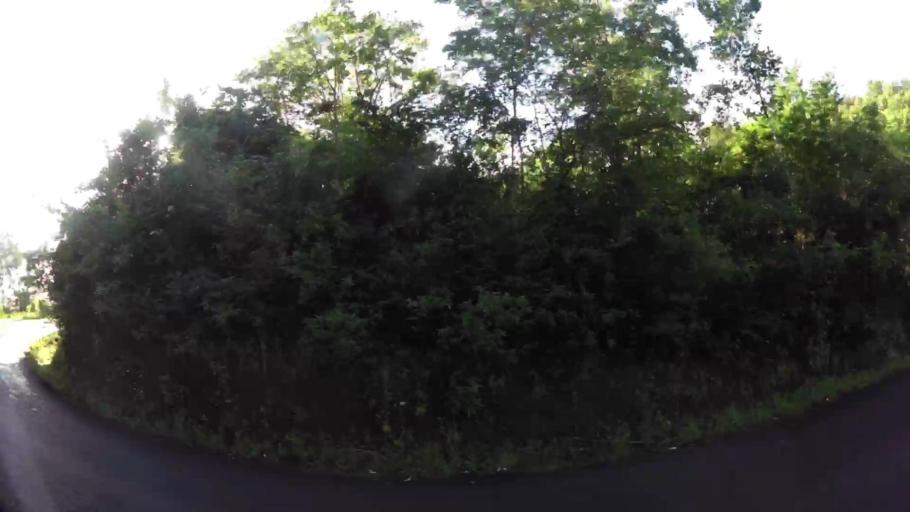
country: LC
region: Anse-la-Raye
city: Anse La Raye
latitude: 13.9249
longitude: -61.0420
